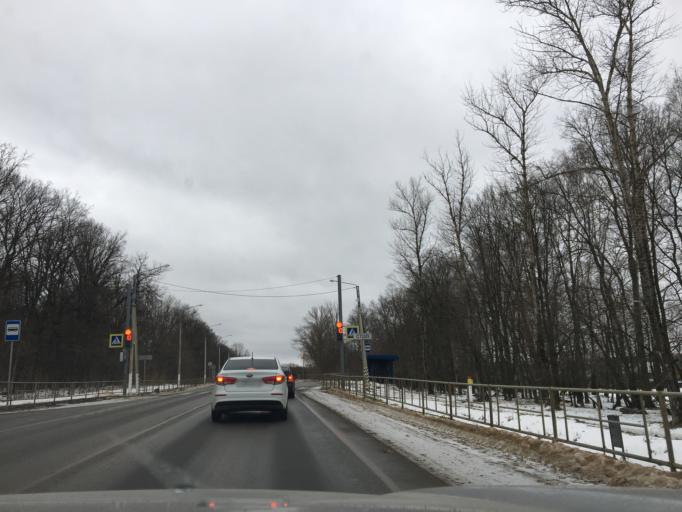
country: RU
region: Tula
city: Pervomayskiy
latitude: 54.0720
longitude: 37.5400
